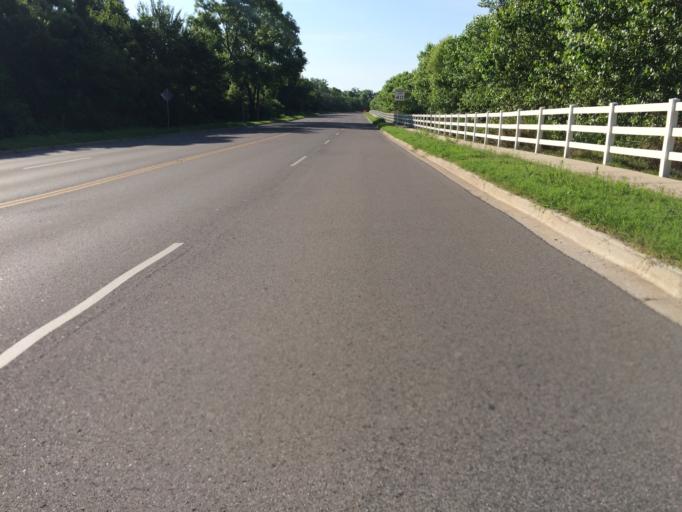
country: US
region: Oklahoma
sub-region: Cleveland County
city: Norman
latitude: 35.2077
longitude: -97.4934
